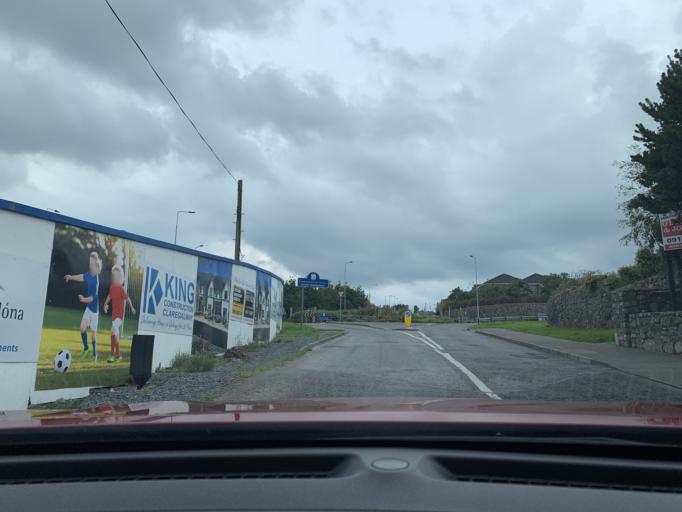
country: IE
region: Connaught
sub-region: County Galway
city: Bearna
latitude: 53.2671
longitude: -9.1175
